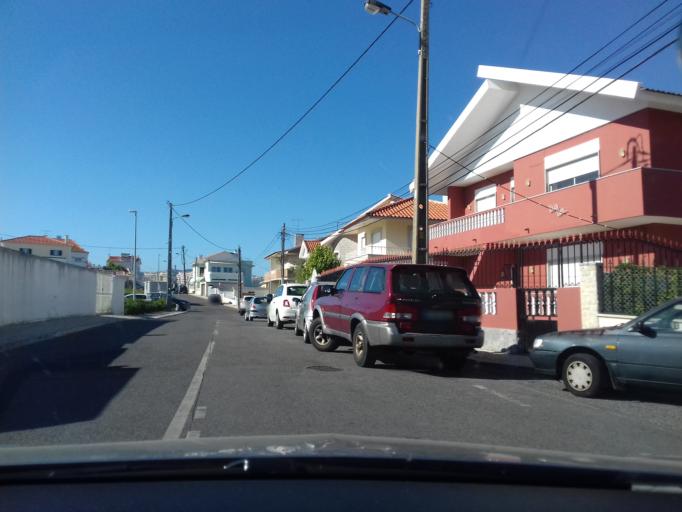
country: PT
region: Lisbon
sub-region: Cascais
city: Alcabideche
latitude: 38.7194
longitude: -9.4096
